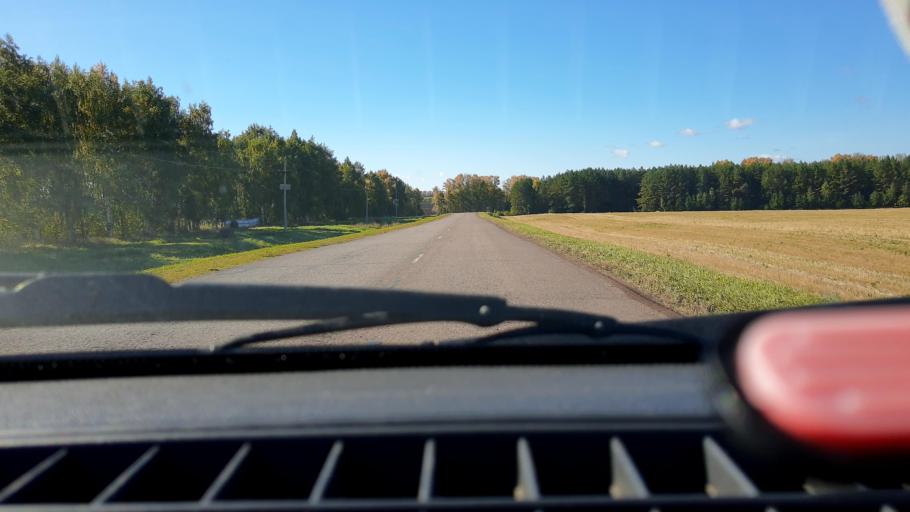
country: RU
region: Bashkortostan
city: Kushnarenkovo
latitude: 55.0669
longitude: 55.4496
